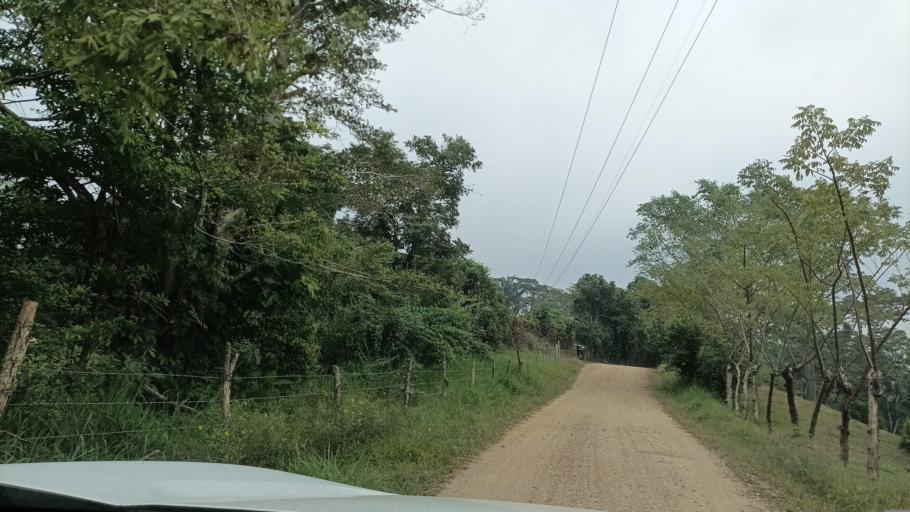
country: MX
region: Veracruz
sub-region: Uxpanapa
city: Poblado 10
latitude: 17.5442
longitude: -94.2356
